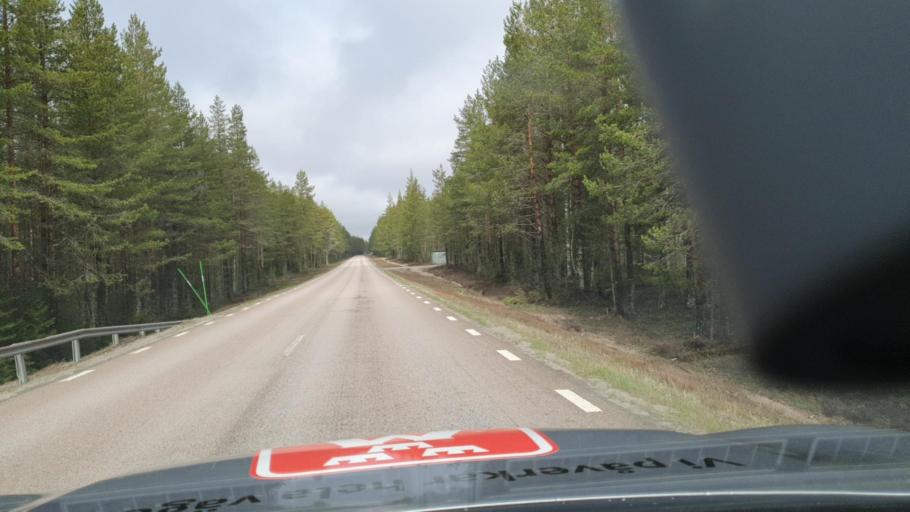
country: SE
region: Vaesternorrland
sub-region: OErnskoeldsviks Kommun
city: Husum
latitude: 63.4211
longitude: 18.9646
